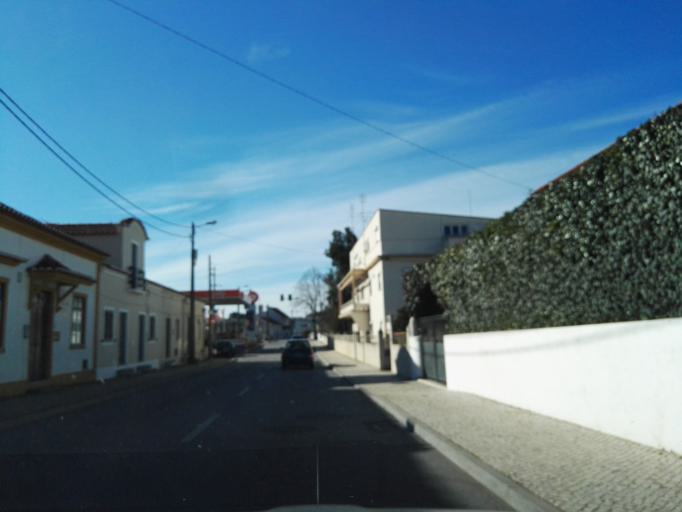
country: PT
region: Santarem
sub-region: Macao
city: Macao
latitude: 39.4643
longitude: -8.0417
